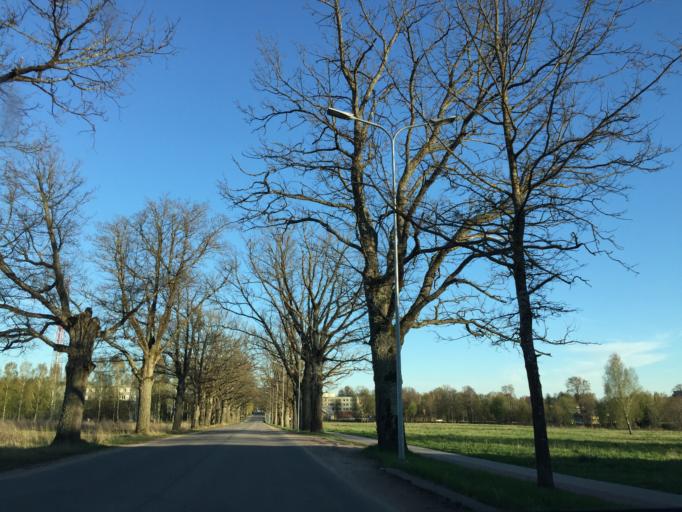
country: LV
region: Valmieras Rajons
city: Valmiera
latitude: 57.5504
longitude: 25.4197
